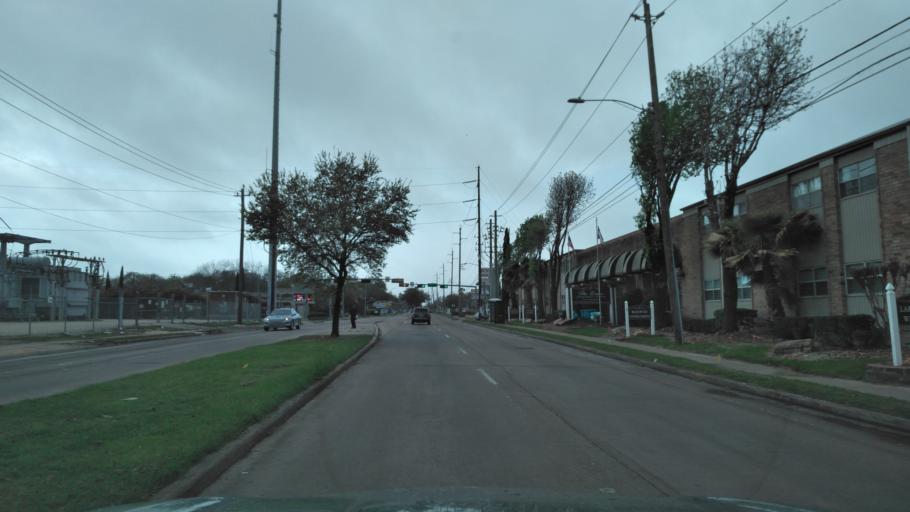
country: US
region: Texas
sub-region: Harris County
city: Hunters Creek Village
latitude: 29.7364
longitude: -95.4843
